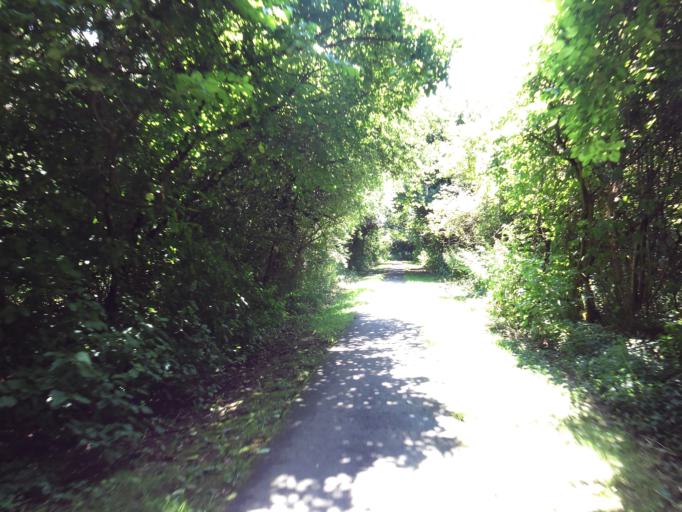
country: NL
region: Limburg
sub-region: Gemeente Voerendaal
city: Voerendaal
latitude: 50.8871
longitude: 5.9329
